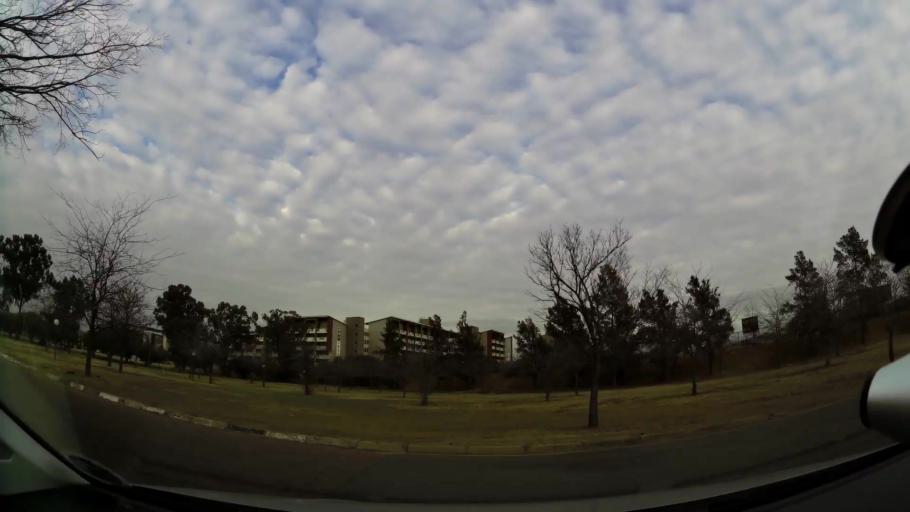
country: ZA
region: Orange Free State
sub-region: Mangaung Metropolitan Municipality
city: Bloemfontein
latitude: -29.1150
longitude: 26.1893
